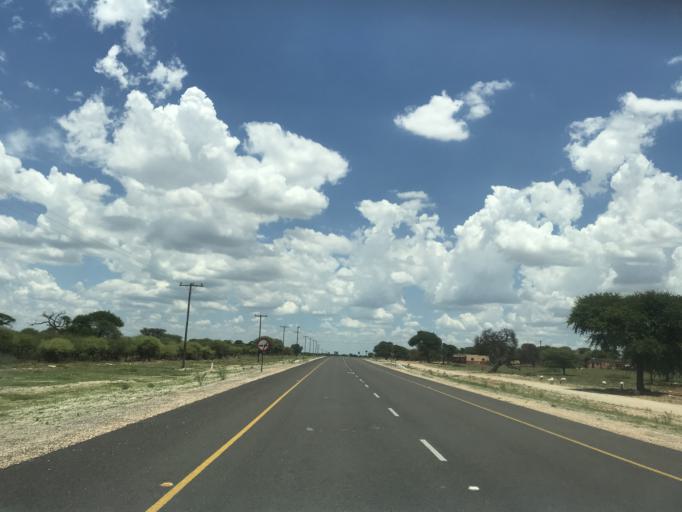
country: BW
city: Mabuli
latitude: -25.7478
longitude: 24.9790
